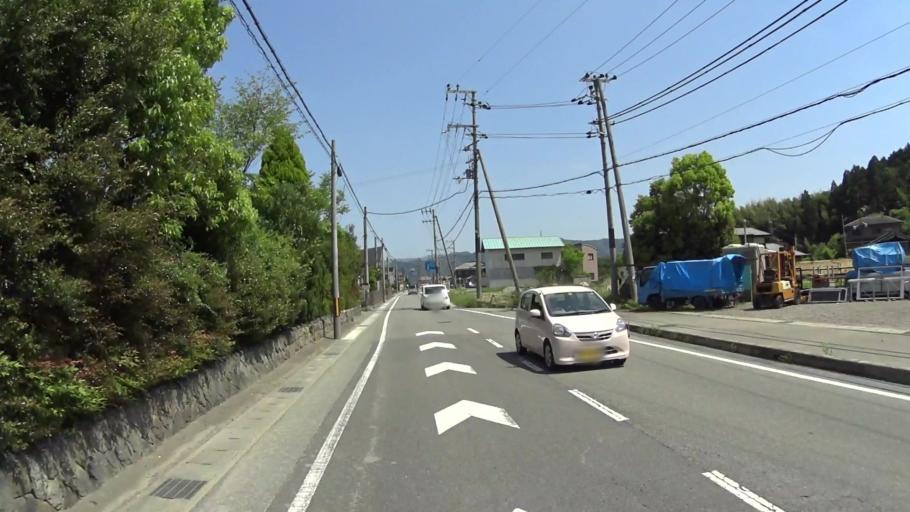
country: JP
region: Kyoto
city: Kameoka
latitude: 35.0210
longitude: 135.5264
